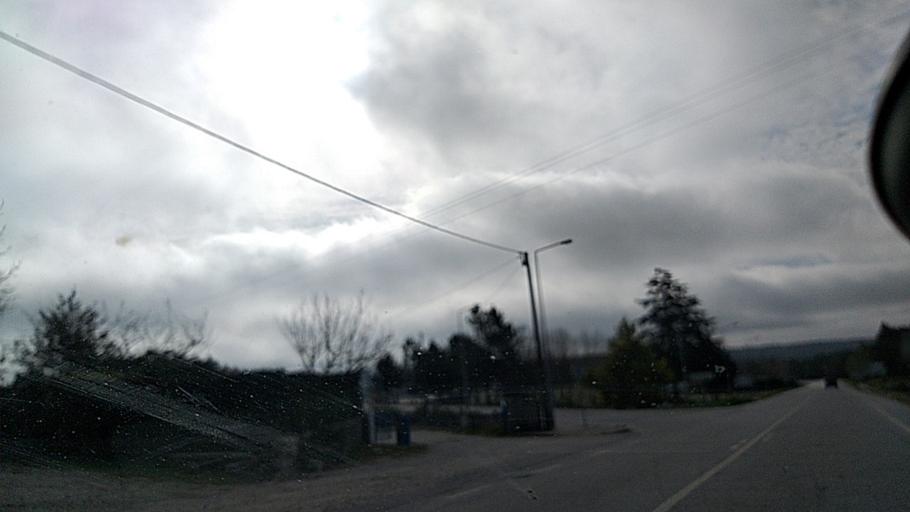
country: PT
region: Guarda
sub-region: Aguiar da Beira
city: Aguiar da Beira
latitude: 40.8163
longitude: -7.5374
